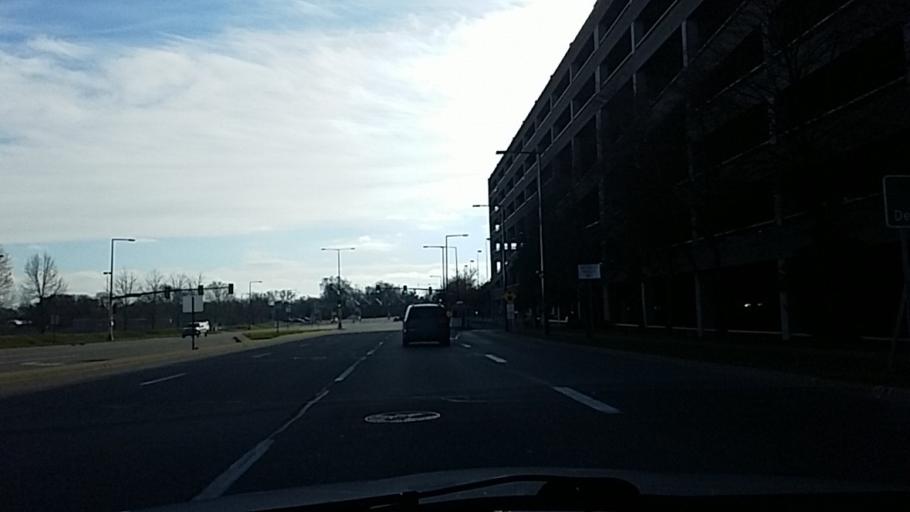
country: US
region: Minnesota
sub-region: Hennepin County
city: Richfield
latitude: 44.8546
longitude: -93.2378
